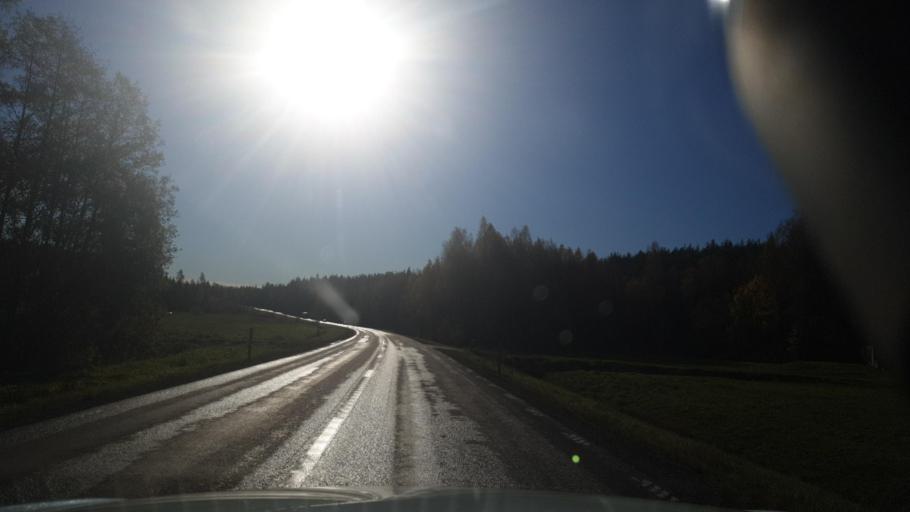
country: SE
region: Vaermland
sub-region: Arvika Kommun
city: Arvika
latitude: 59.5557
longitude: 12.7253
